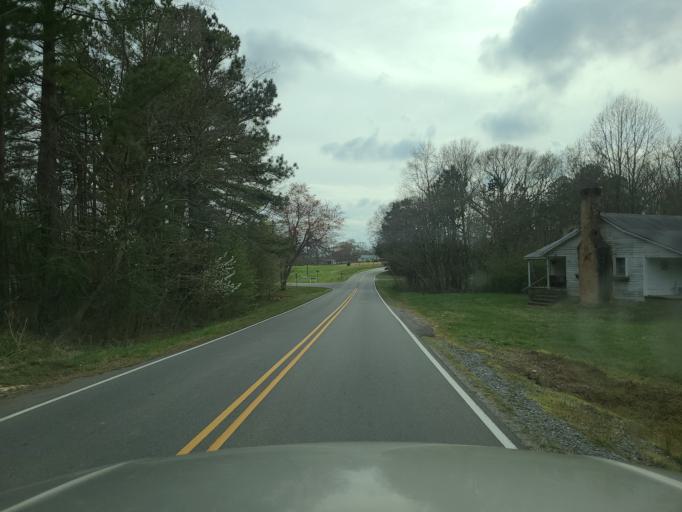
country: US
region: North Carolina
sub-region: Cleveland County
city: Boiling Springs
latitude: 35.2416
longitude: -81.7378
